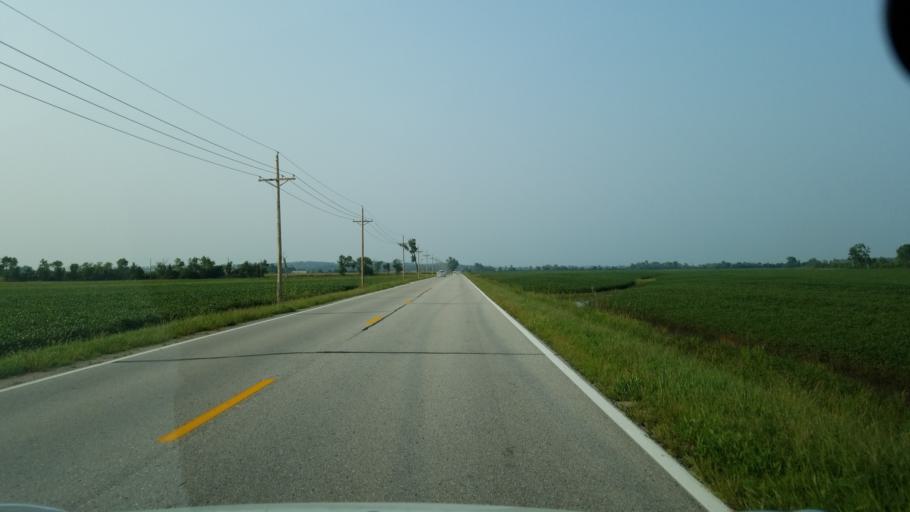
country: US
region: Nebraska
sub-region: Sarpy County
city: Offutt Air Force Base
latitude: 41.0935
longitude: -95.8898
